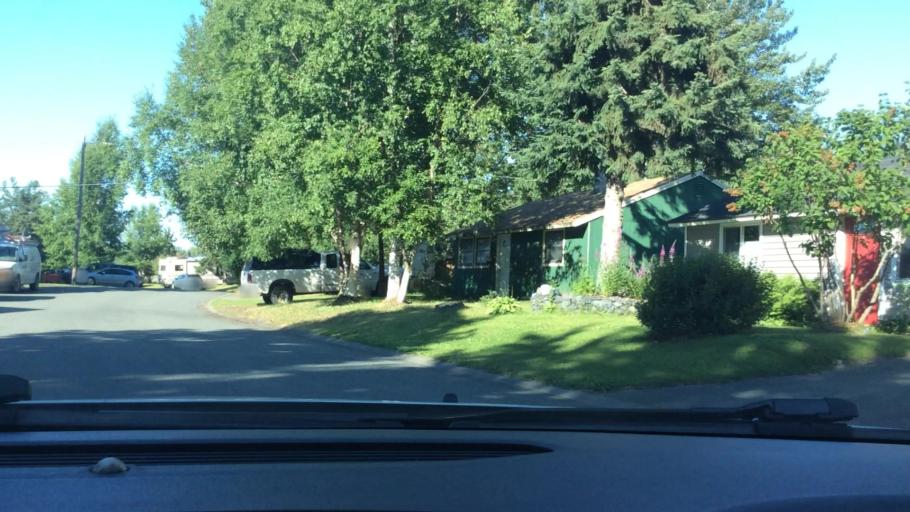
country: US
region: Alaska
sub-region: Anchorage Municipality
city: Anchorage
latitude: 61.2045
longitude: -149.7693
